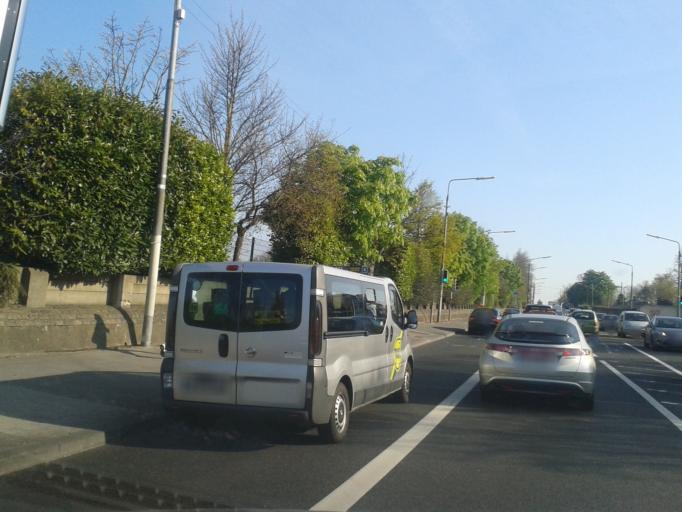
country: IE
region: Leinster
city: Drumcondra
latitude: 53.3773
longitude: -6.2487
